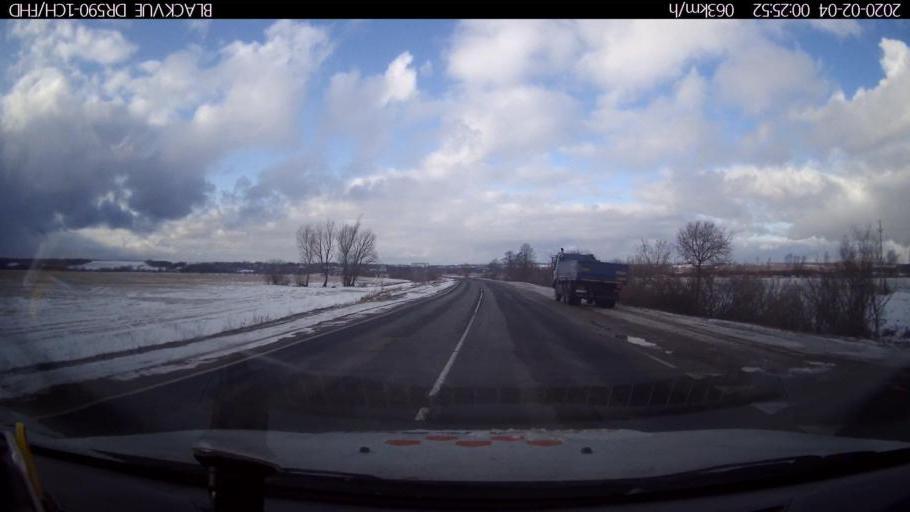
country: RU
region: Nizjnij Novgorod
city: Kstovo
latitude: 56.0098
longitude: 44.2068
